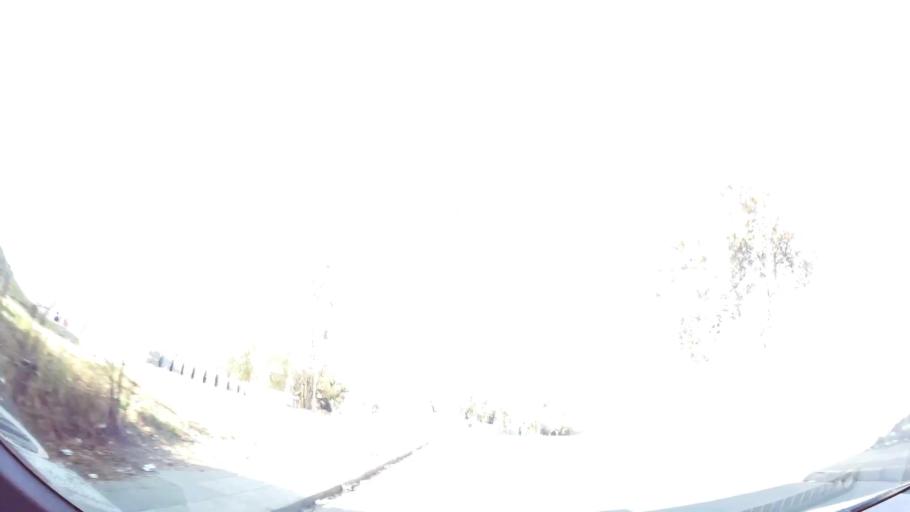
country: ZA
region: Gauteng
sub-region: Ekurhuleni Metropolitan Municipality
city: Boksburg
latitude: -26.2192
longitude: 28.2435
